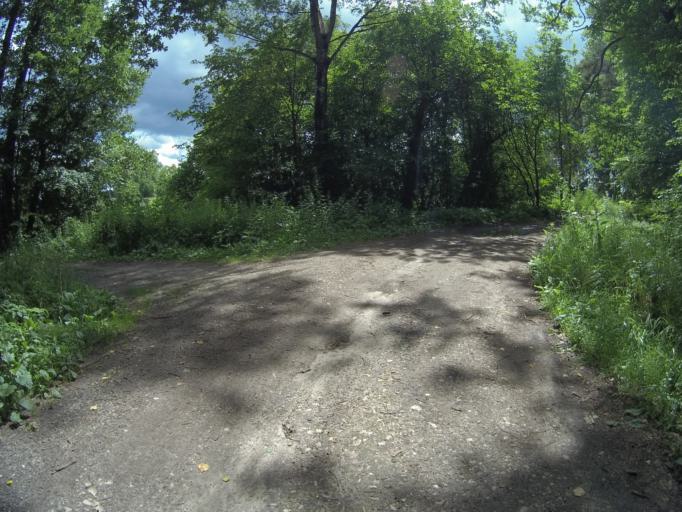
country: RU
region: Vladimir
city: Raduzhnyy
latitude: 56.0527
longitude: 40.3066
